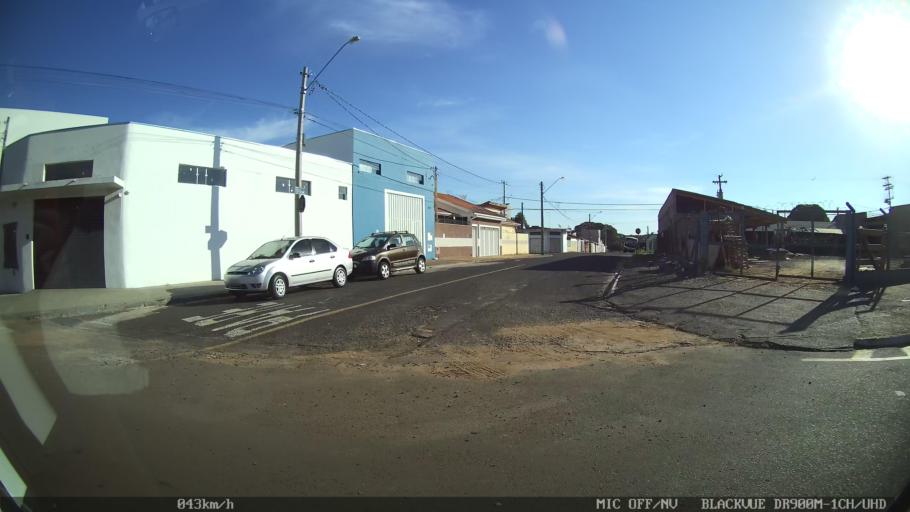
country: BR
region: Sao Paulo
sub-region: Franca
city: Franca
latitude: -20.5161
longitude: -47.3729
